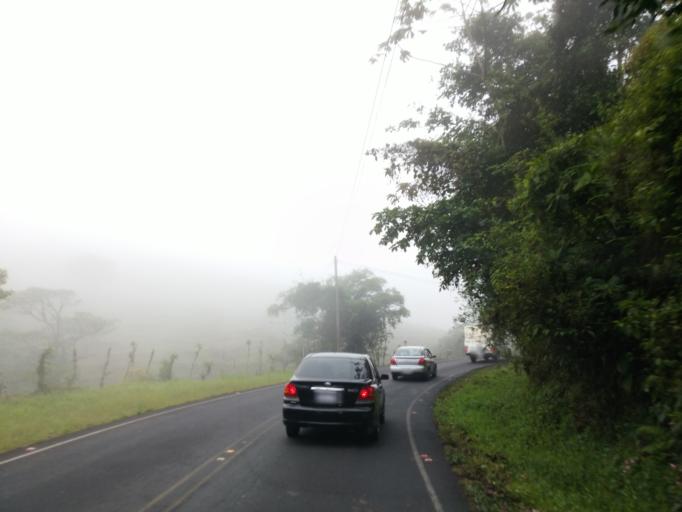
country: CR
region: Alajuela
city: San Ramon
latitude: 10.1777
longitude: -84.5013
